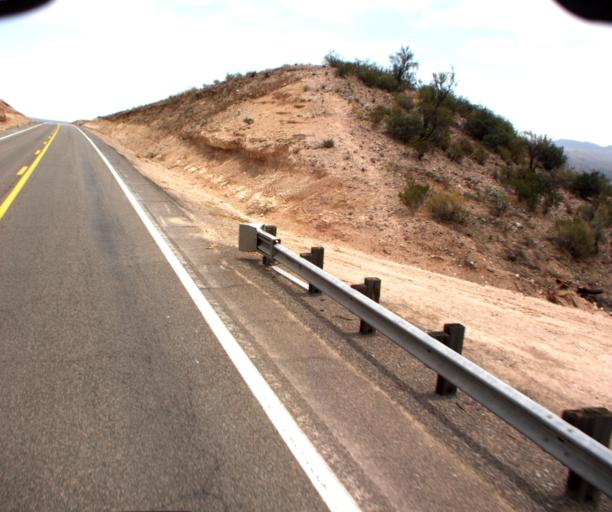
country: US
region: Arizona
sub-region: Graham County
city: Bylas
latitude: 33.2143
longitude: -110.2114
